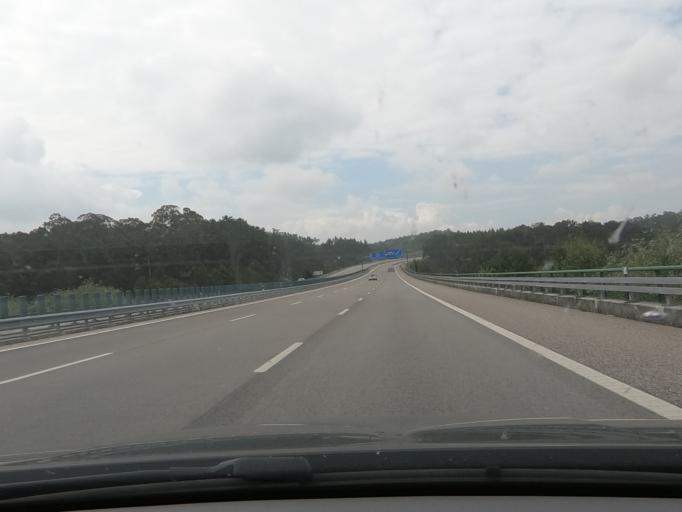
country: PT
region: Leiria
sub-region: Leiria
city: Souto da Carpalhosa
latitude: 39.8664
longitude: -8.8247
